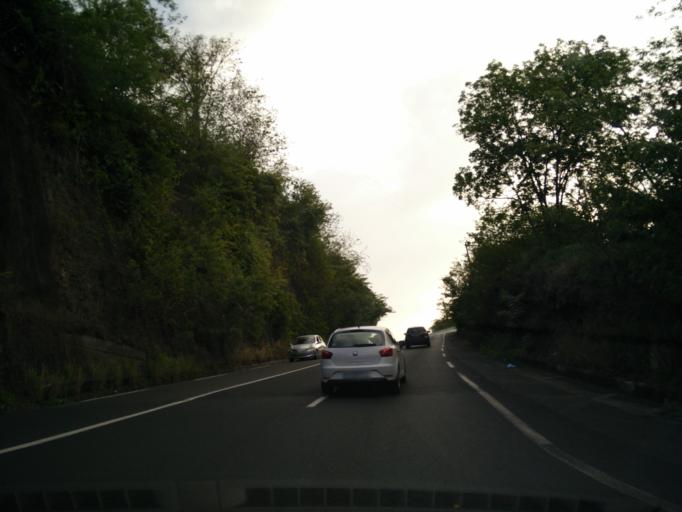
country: MQ
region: Martinique
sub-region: Martinique
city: Fort-de-France
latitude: 14.6406
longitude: -61.1356
